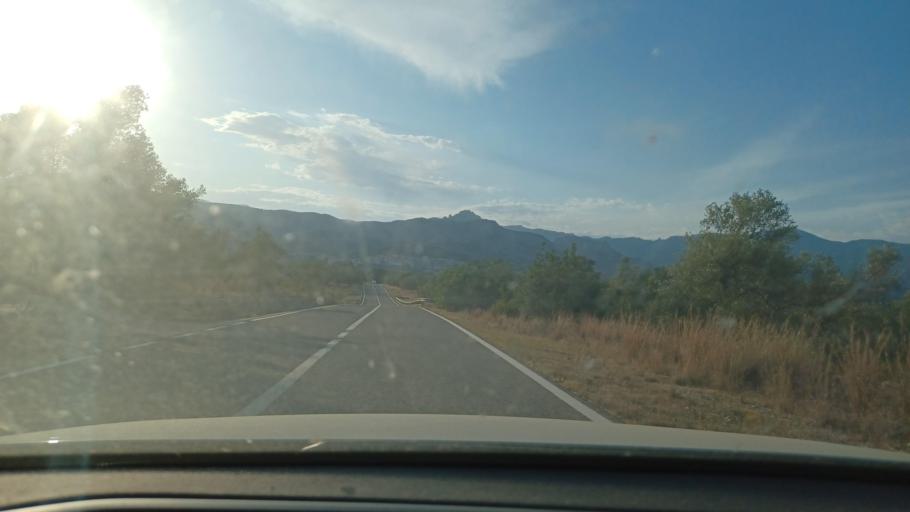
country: ES
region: Catalonia
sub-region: Provincia de Tarragona
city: Mas de Barberans
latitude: 40.7248
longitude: 0.3905
